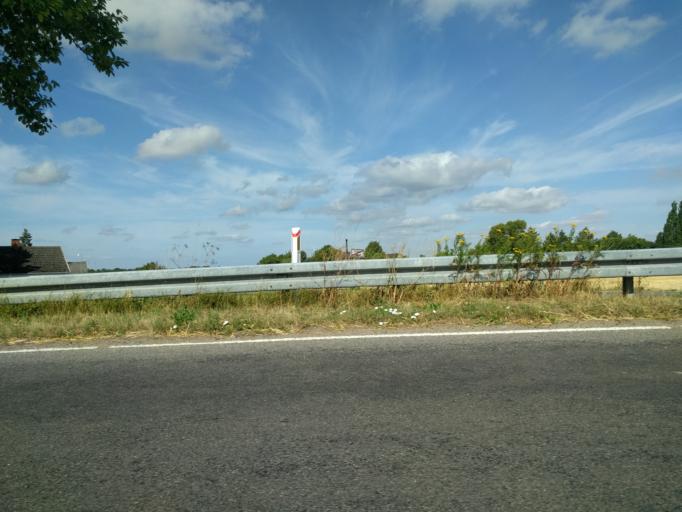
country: DK
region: Zealand
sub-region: Vordingborg Kommune
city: Stege
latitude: 54.9590
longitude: 12.2408
